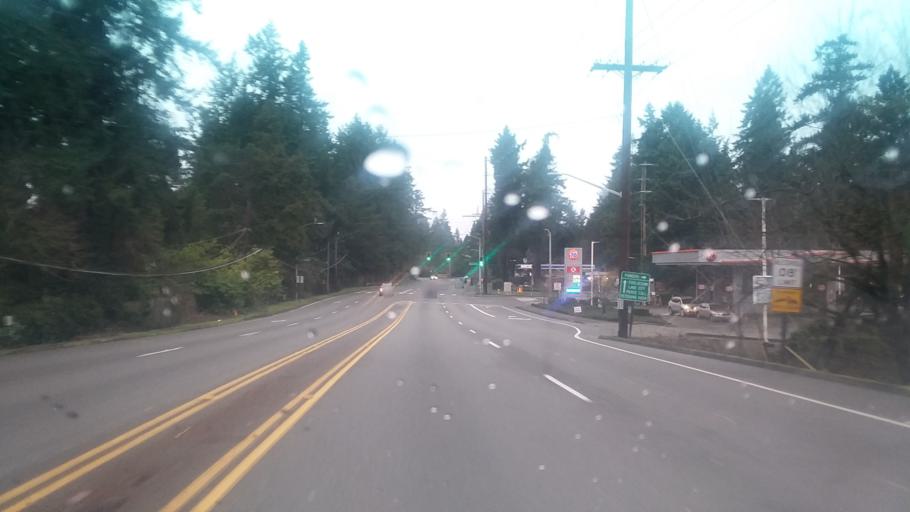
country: US
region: Washington
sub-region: Pierce County
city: McChord Air Force Base
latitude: 47.1379
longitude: -122.5260
